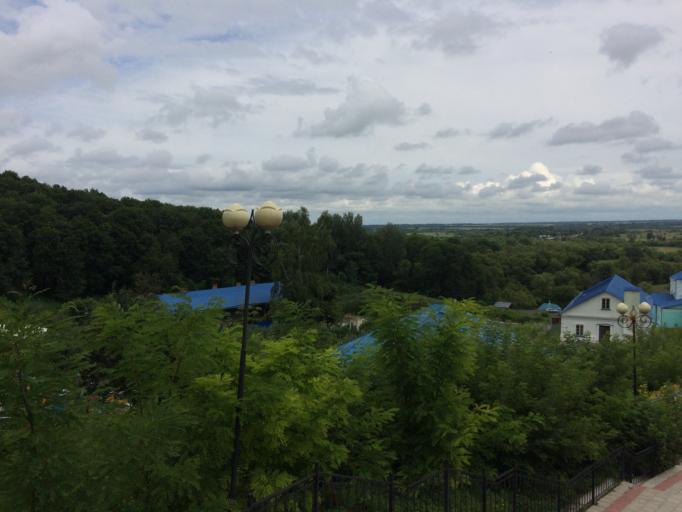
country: RU
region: Kursk
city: Zolotukhino
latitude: 51.9729
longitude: 36.3135
